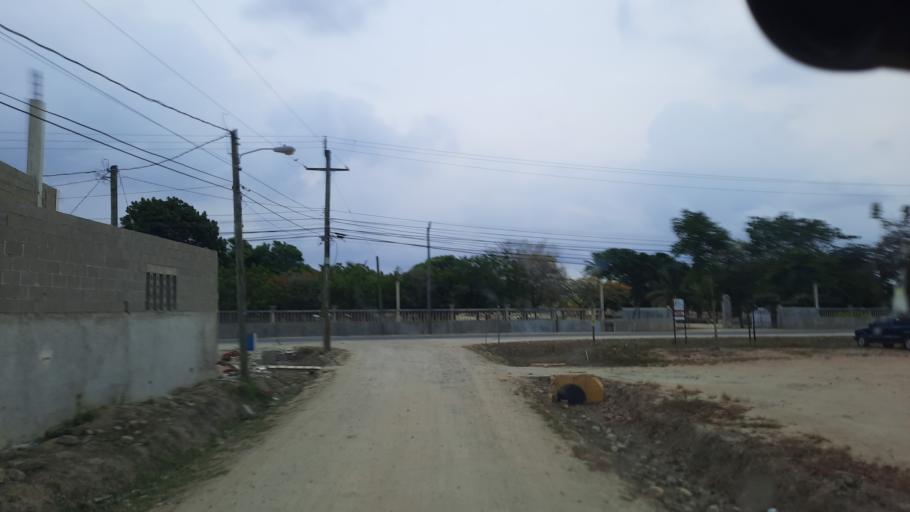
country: BZ
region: Stann Creek
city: Placencia
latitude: 16.5350
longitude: -88.4241
